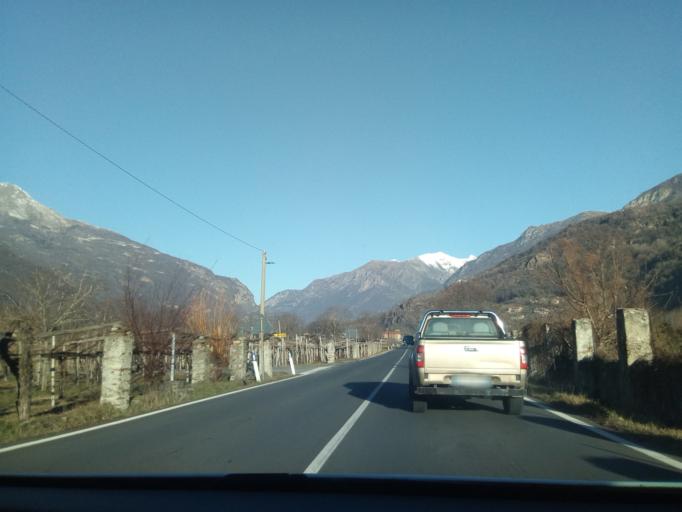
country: IT
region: Piedmont
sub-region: Provincia di Torino
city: Borgofranco d'Ivrea
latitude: 45.5261
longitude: 7.8502
